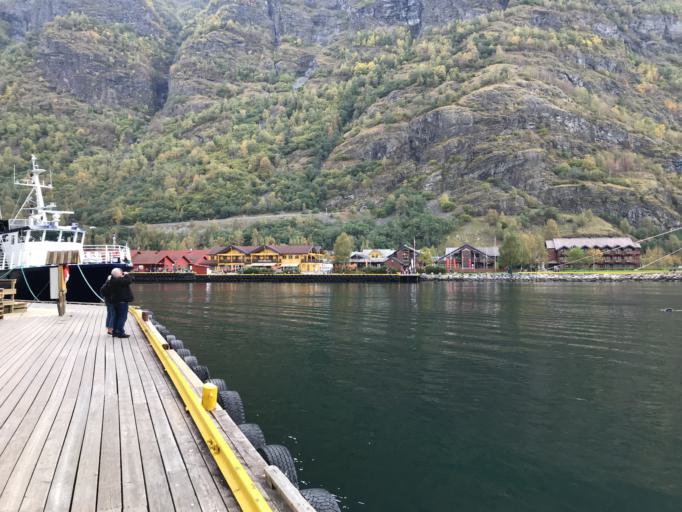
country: NO
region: Sogn og Fjordane
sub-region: Aurland
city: Aurlandsvangen
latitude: 60.8618
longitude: 7.1181
